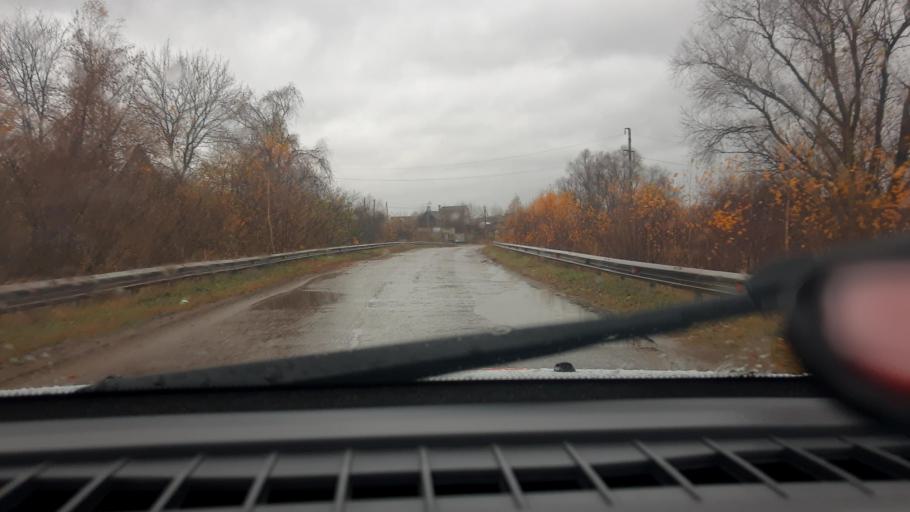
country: RU
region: Nizjnij Novgorod
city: Kstovo
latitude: 56.1451
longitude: 44.1545
